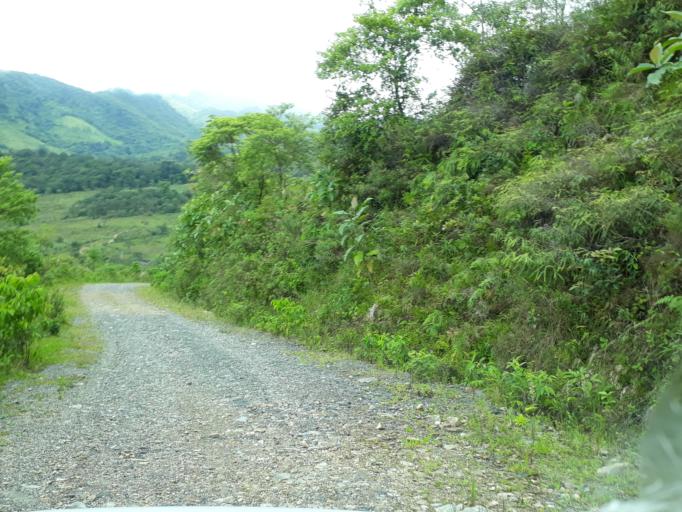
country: CO
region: Cundinamarca
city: Gachala
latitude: 4.7115
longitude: -73.3667
